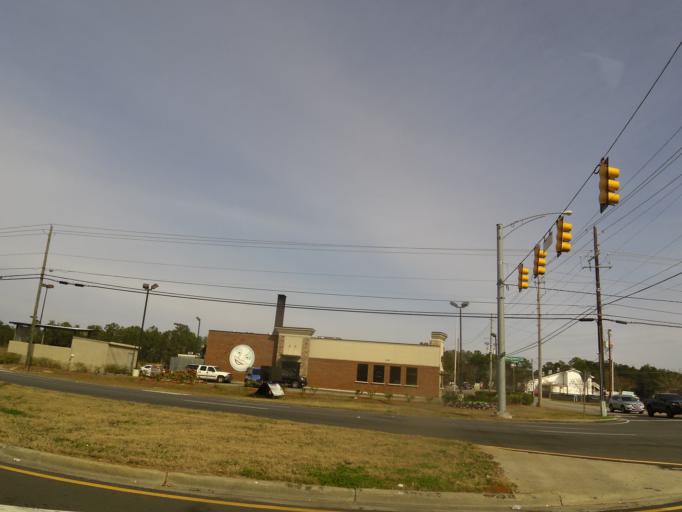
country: US
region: Alabama
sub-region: Houston County
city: Dothan
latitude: 31.2593
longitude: -85.4358
